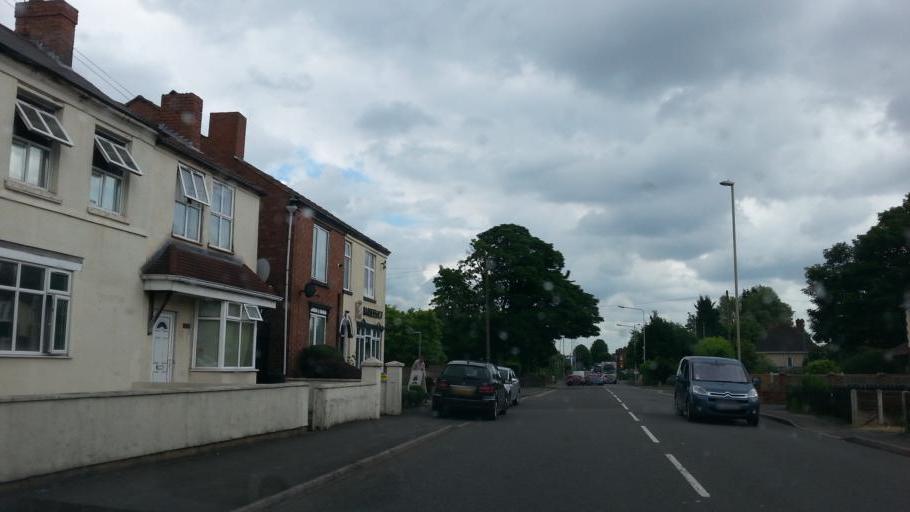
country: GB
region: England
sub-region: Sandwell
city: Tipton
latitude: 52.5319
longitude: -2.0884
